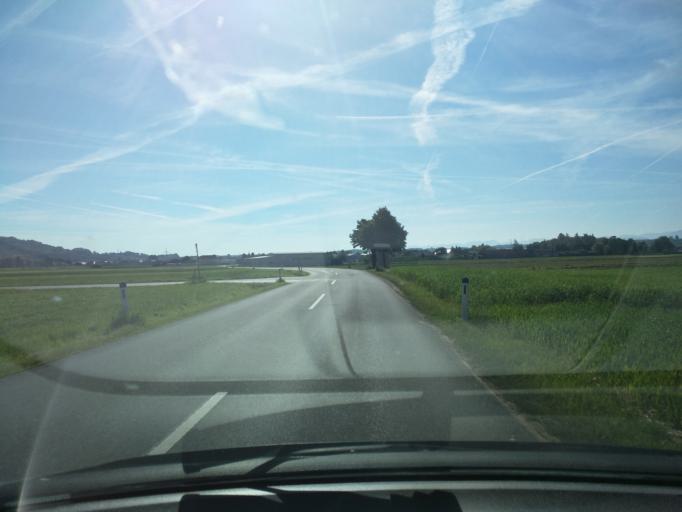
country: AT
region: Lower Austria
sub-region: Politischer Bezirk Melk
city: Blindenmarkt
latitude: 48.1302
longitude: 14.9717
